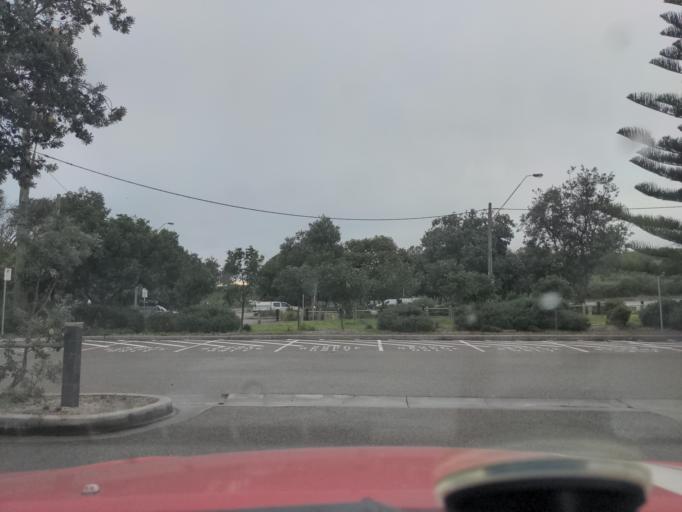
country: AU
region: New South Wales
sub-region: Randwick
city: Malabar
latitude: -33.9514
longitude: 151.2553
